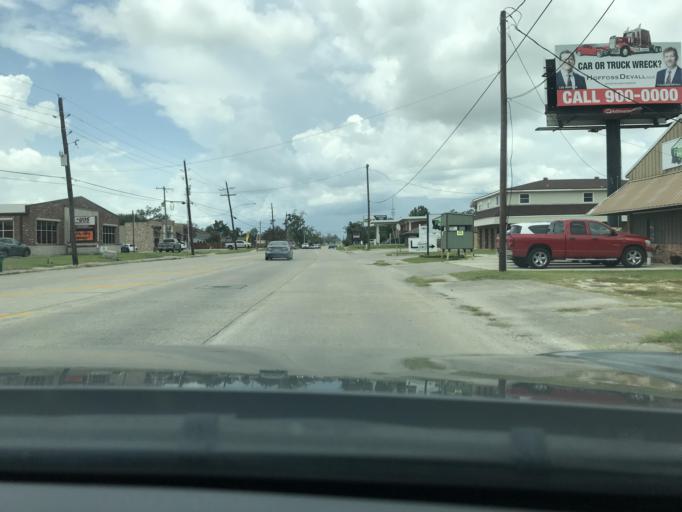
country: US
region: Louisiana
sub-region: Calcasieu Parish
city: Sulphur
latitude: 30.2278
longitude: -93.3266
